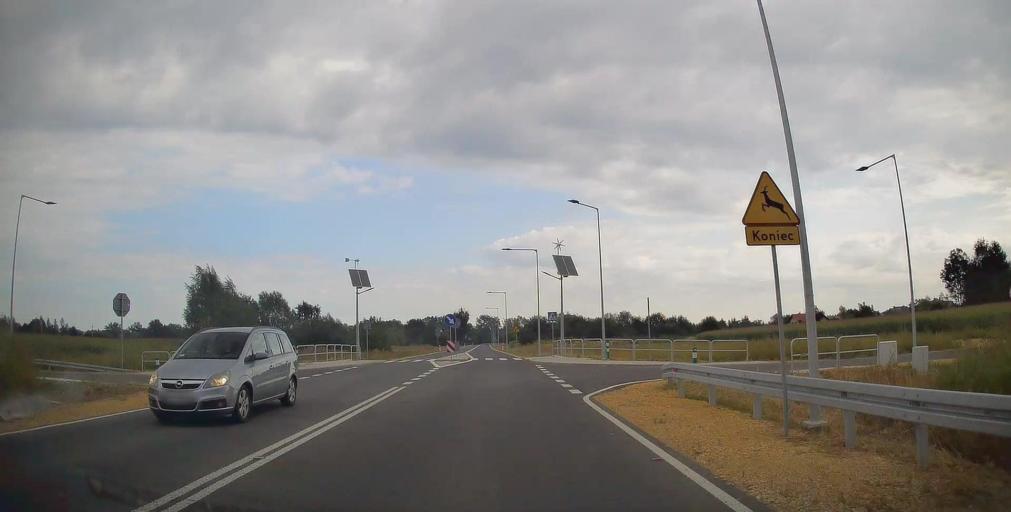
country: PL
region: Lesser Poland Voivodeship
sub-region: Powiat oswiecimski
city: Zator
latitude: 50.0201
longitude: 19.4307
